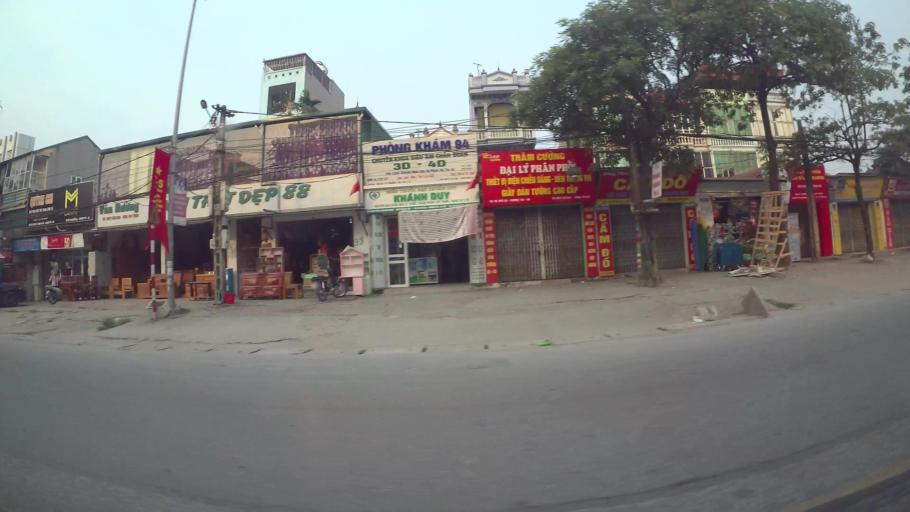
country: VN
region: Ha Noi
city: Thuong Tin
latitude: 20.8741
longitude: 105.8632
